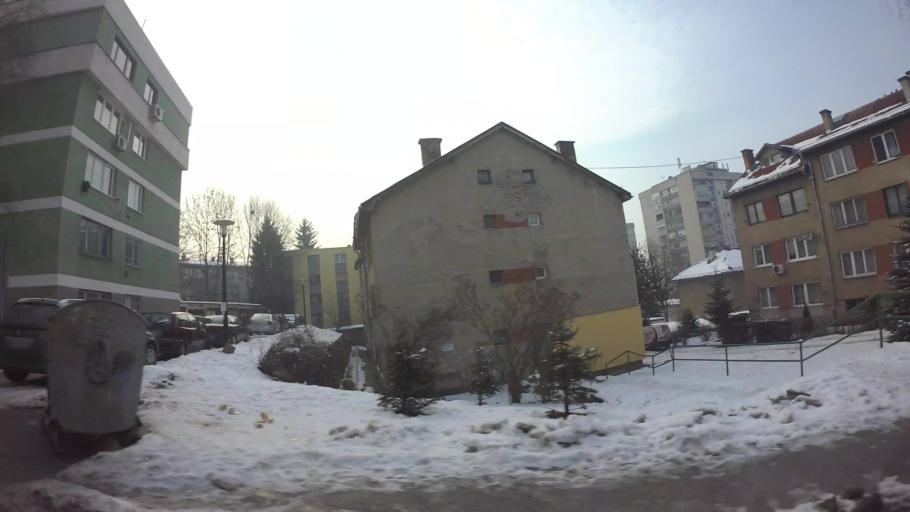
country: BA
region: Federation of Bosnia and Herzegovina
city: Kobilja Glava
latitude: 43.8682
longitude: 18.4198
